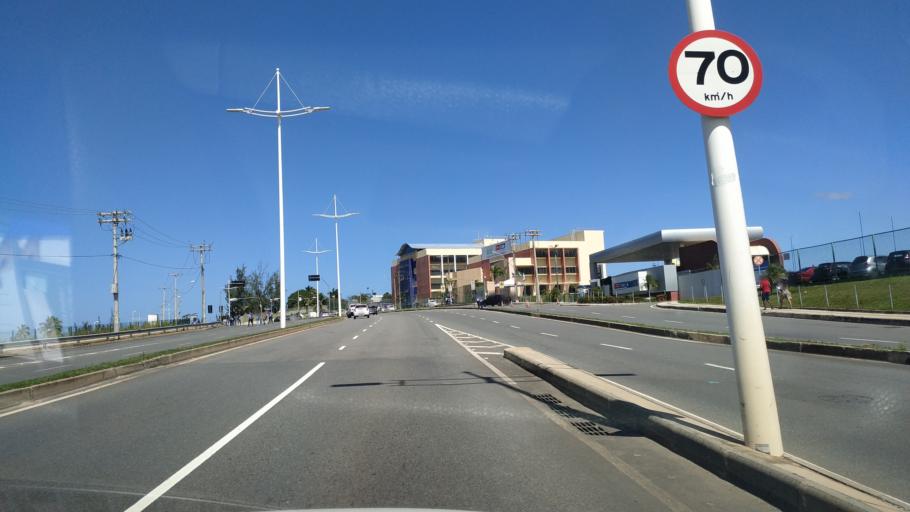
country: BR
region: Bahia
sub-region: Lauro De Freitas
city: Lauro de Freitas
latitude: -12.9387
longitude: -38.3862
